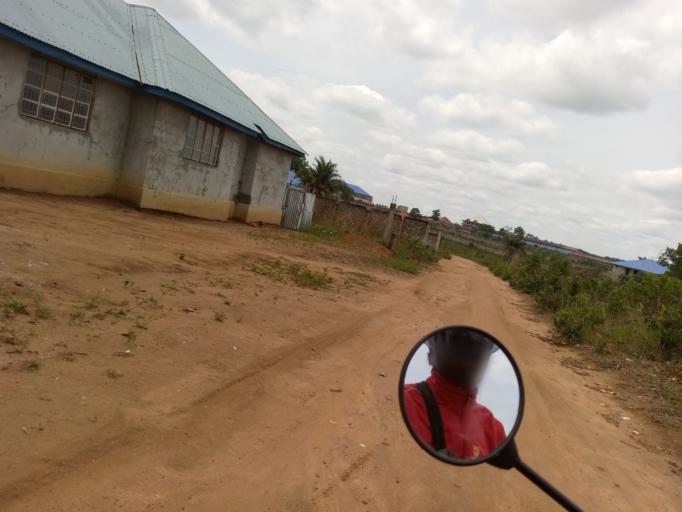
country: SL
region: Western Area
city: Waterloo
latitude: 8.3291
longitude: -13.0323
